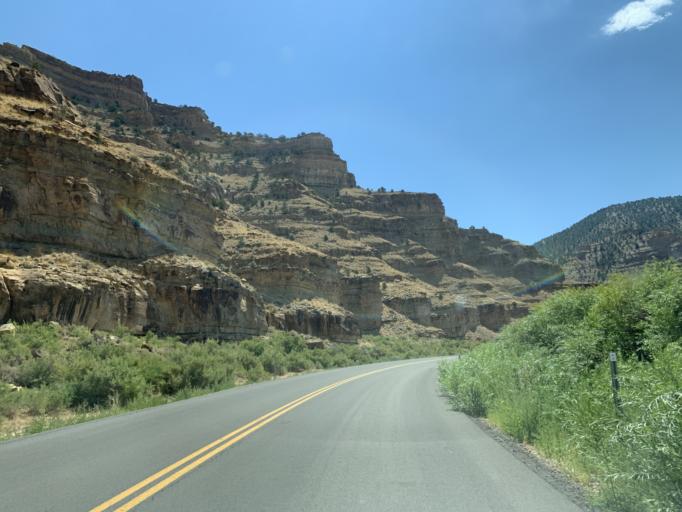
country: US
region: Utah
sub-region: Carbon County
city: East Carbon City
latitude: 39.8125
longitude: -110.2745
